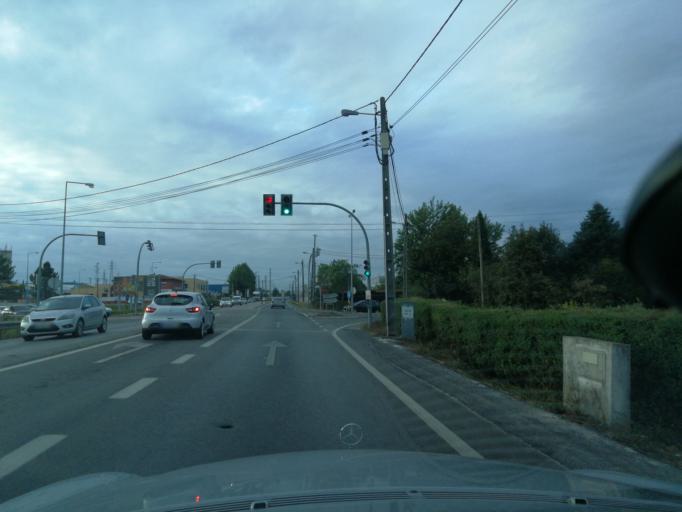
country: PT
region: Aveiro
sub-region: Agueda
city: Agueda
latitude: 40.5905
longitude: -8.4525
